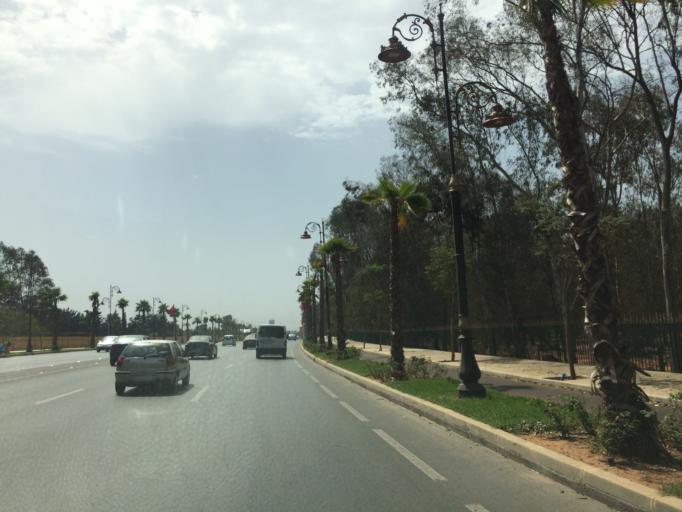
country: MA
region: Rabat-Sale-Zemmour-Zaer
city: Sale
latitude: 34.0335
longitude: -6.7798
